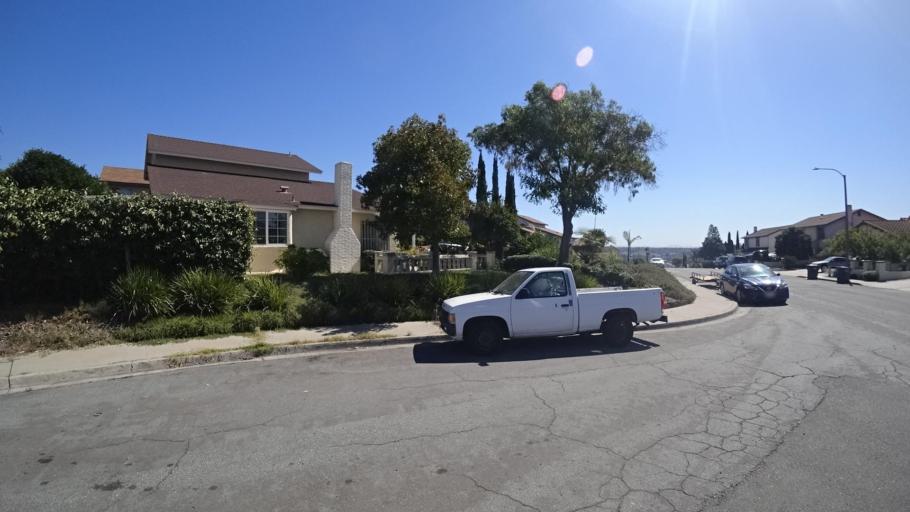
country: US
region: California
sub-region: San Diego County
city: La Presa
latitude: 32.6961
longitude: -117.0172
